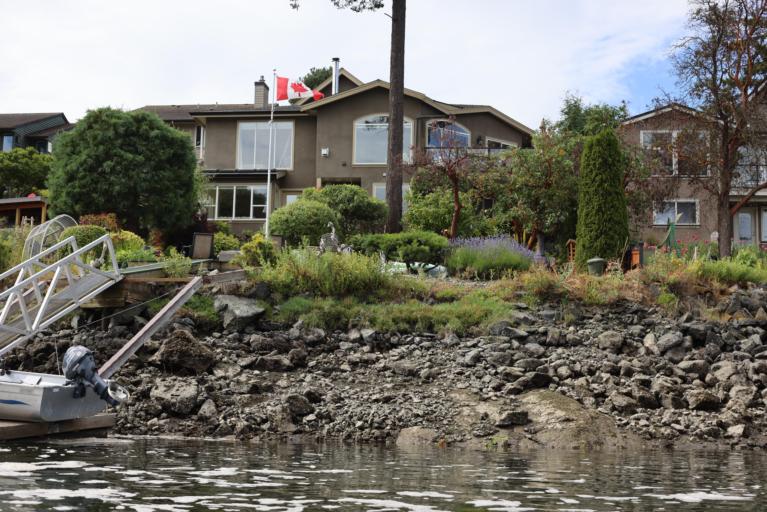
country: CA
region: British Columbia
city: Victoria
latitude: 48.4433
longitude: -123.3956
